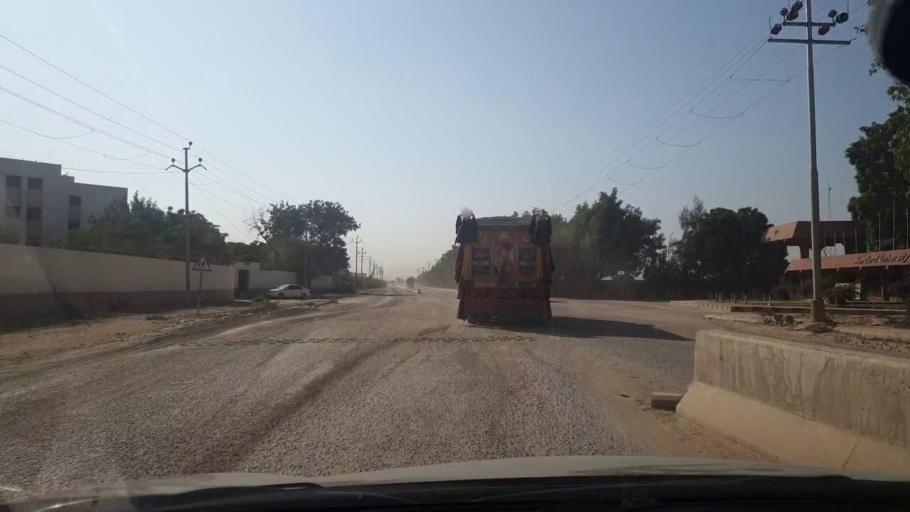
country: PK
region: Sindh
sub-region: Karachi District
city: Karachi
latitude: 25.0840
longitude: 67.0126
